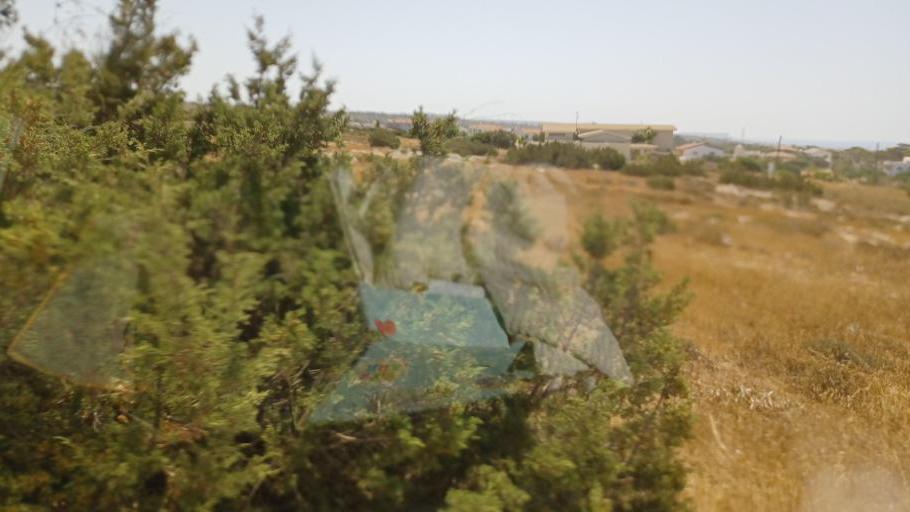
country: CY
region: Ammochostos
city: Paralimni
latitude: 35.0071
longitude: 33.9689
